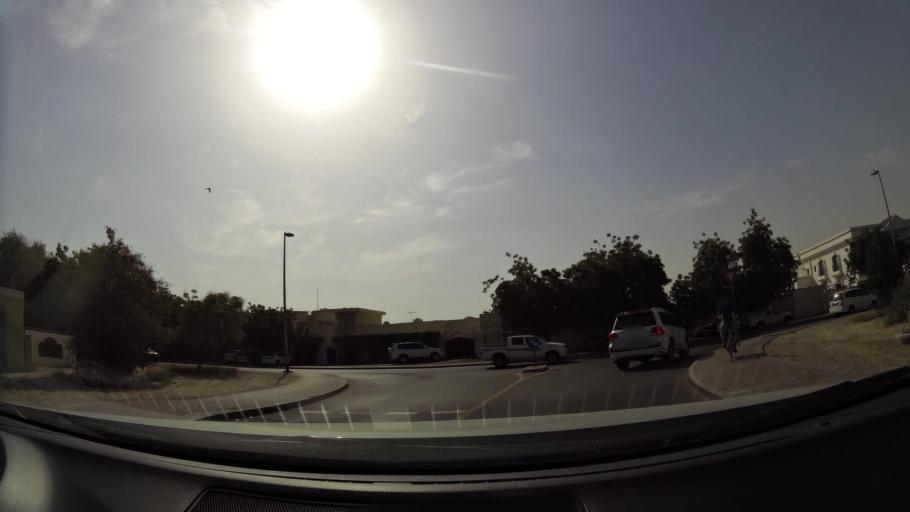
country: AE
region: Ash Shariqah
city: Sharjah
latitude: 25.2213
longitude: 55.3878
